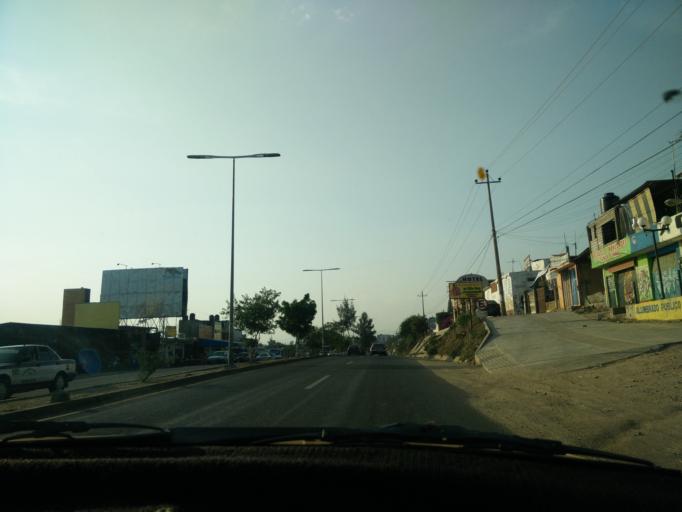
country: MX
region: Oaxaca
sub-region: Santa Maria Atzompa
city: San Jeronimo Yahuiche
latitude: 17.1087
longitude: -96.7548
